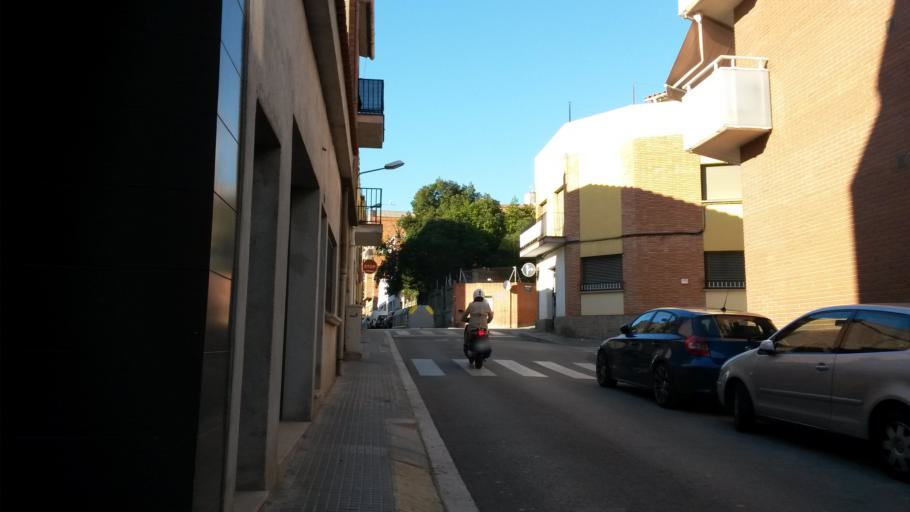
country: ES
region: Catalonia
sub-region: Provincia de Barcelona
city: Cerdanyola del Valles
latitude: 41.4902
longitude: 2.1330
